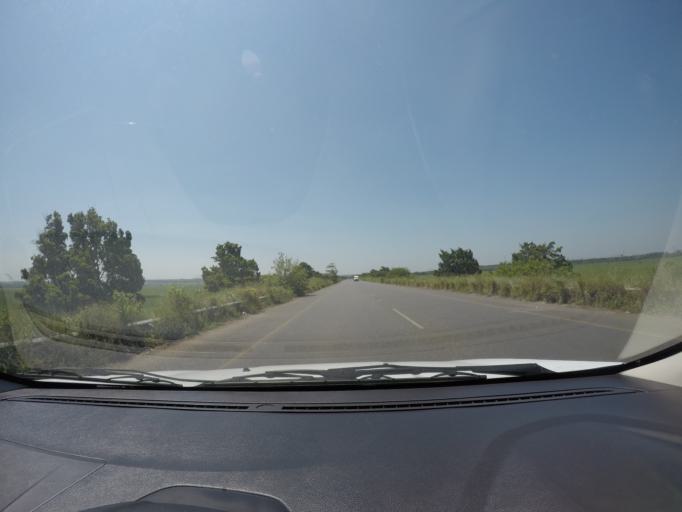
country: ZA
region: KwaZulu-Natal
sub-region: uThungulu District Municipality
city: Empangeni
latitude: -28.7885
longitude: 31.9581
